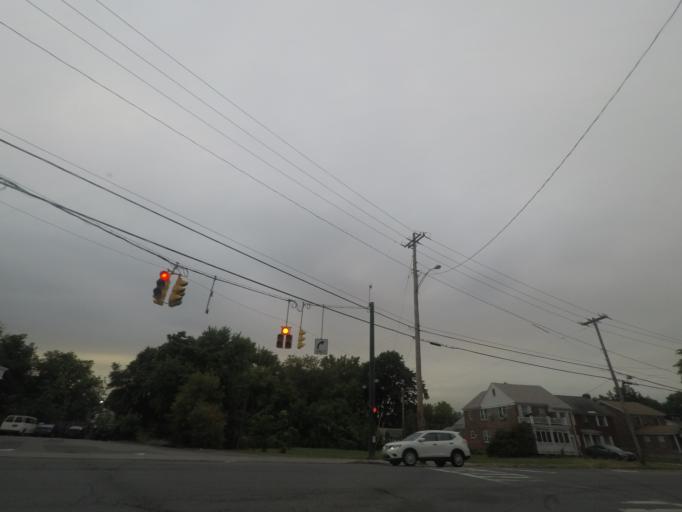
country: US
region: New York
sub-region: Albany County
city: Delmar
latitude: 42.6551
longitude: -73.8172
